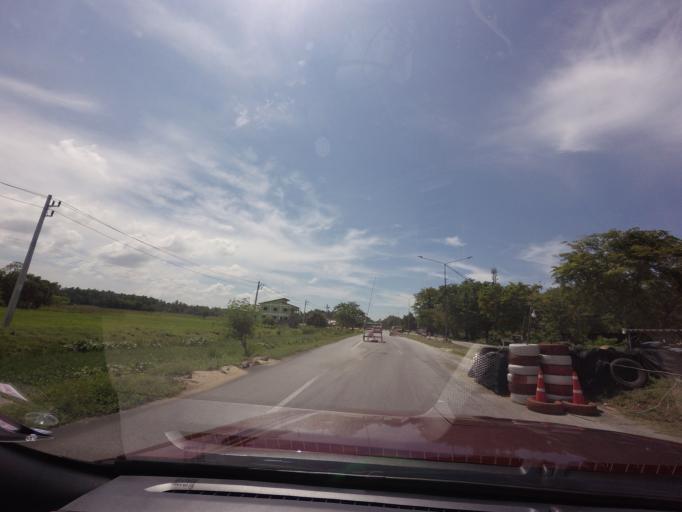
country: TH
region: Pattani
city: Mai Kaen
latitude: 6.5831
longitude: 101.6370
